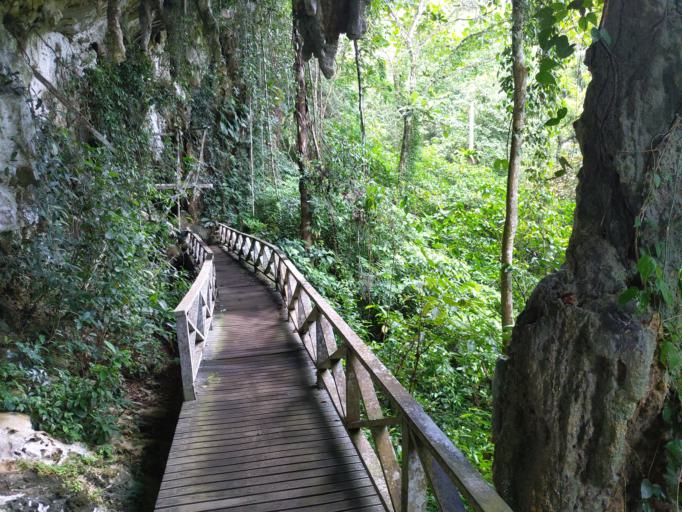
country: MY
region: Sarawak
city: Miri
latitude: 3.8186
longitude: 113.7811
